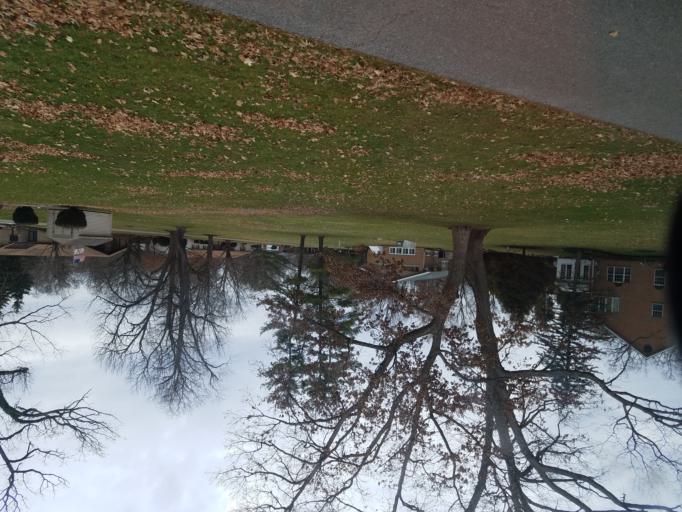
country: US
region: Ohio
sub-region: Marion County
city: Marion
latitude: 40.5652
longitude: -83.0820
